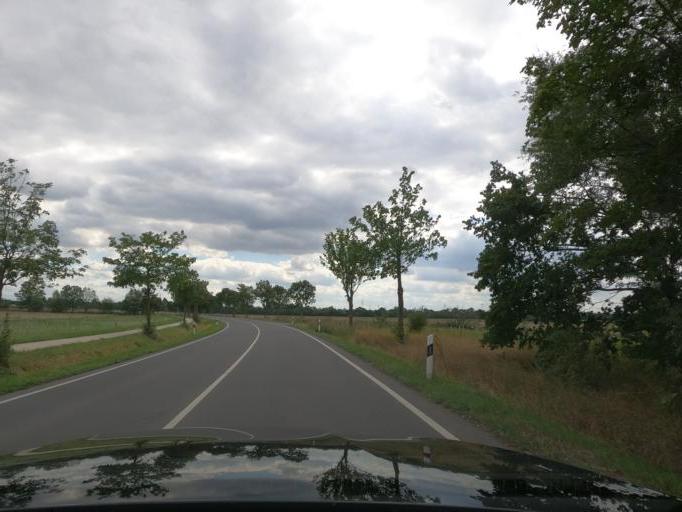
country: DE
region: Lower Saxony
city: Sehnde
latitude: 52.3153
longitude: 10.0282
